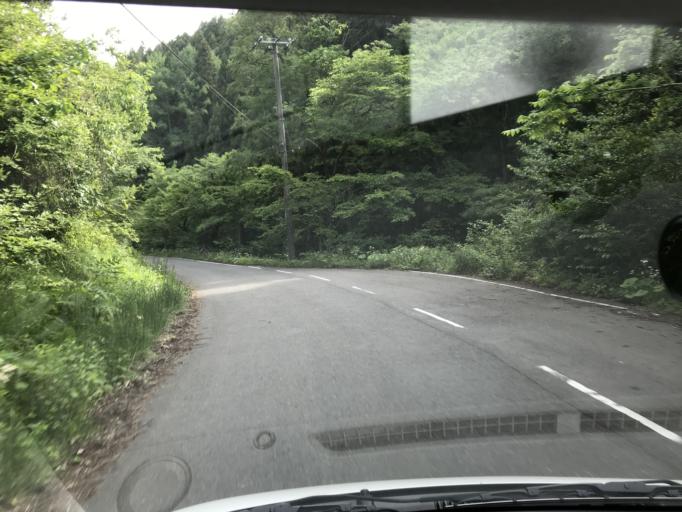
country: JP
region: Miyagi
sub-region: Oshika Gun
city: Onagawa Cho
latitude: 38.6751
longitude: 141.3469
